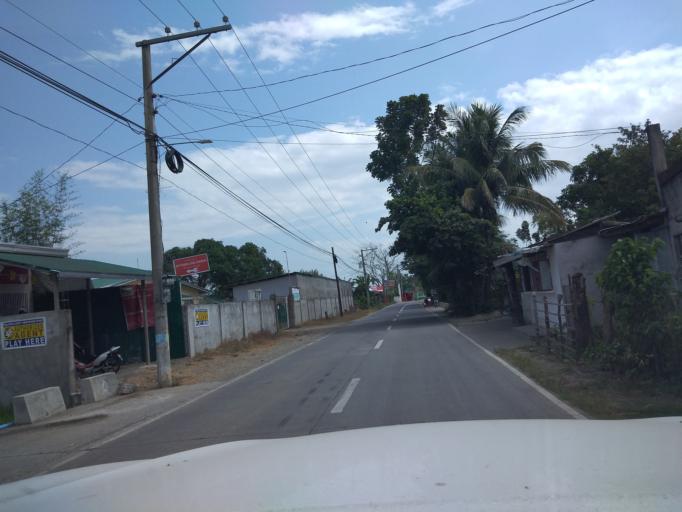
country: PH
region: Central Luzon
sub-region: Province of Pampanga
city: Talang
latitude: 15.0265
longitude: 120.8327
